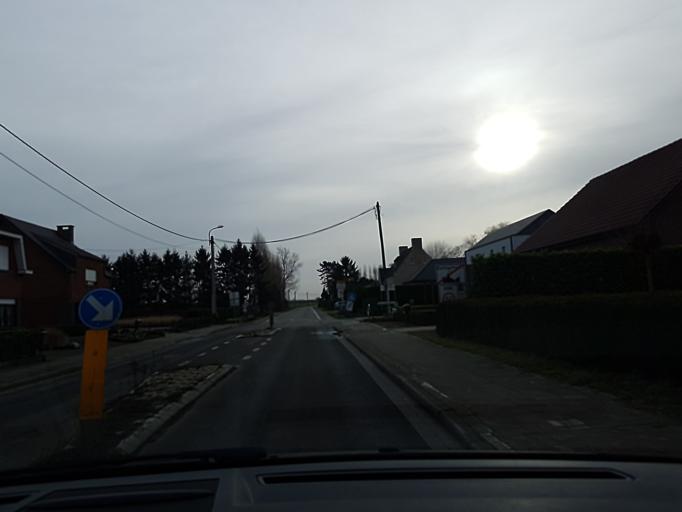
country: BE
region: Flanders
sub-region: Provincie Antwerpen
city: Putte
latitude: 51.0862
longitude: 4.6160
